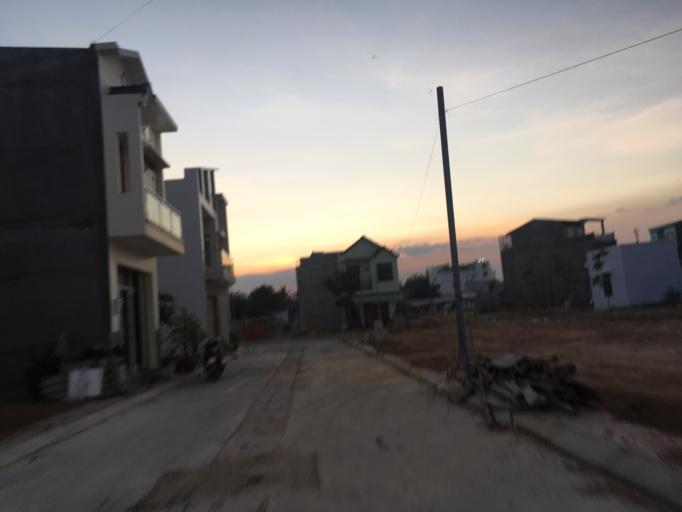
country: VN
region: Ninh Thuan
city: Phan Rang-Thap Cham
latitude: 11.5764
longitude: 108.9968
